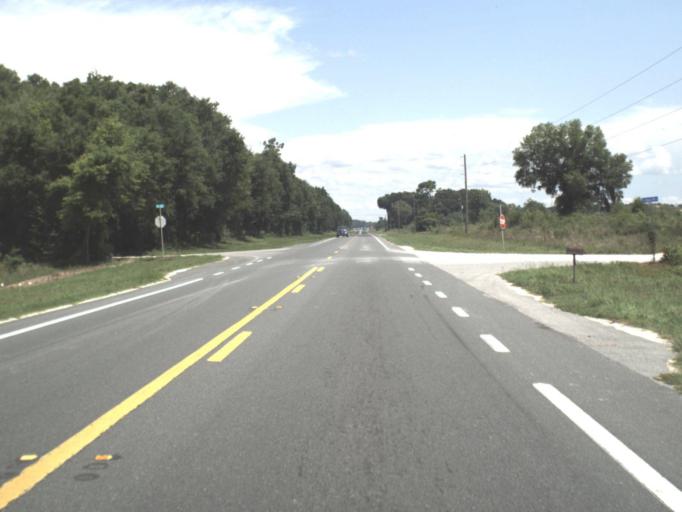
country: US
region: Florida
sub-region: Lafayette County
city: Mayo
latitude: 30.0934
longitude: -83.2322
